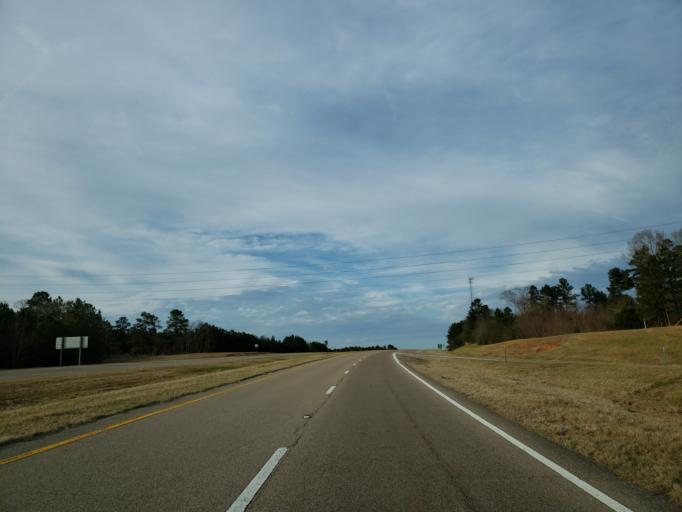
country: US
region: Mississippi
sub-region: Wayne County
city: Waynesboro
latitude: 31.6852
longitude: -88.6169
